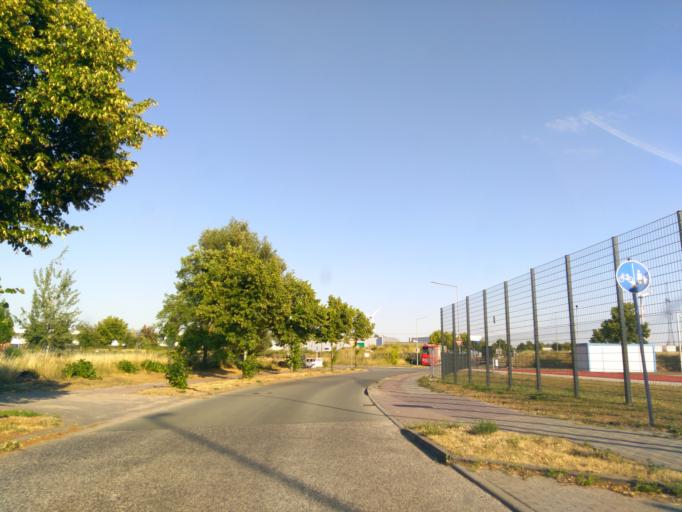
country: DE
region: Brandenburg
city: Nauen
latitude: 52.5995
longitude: 12.8907
